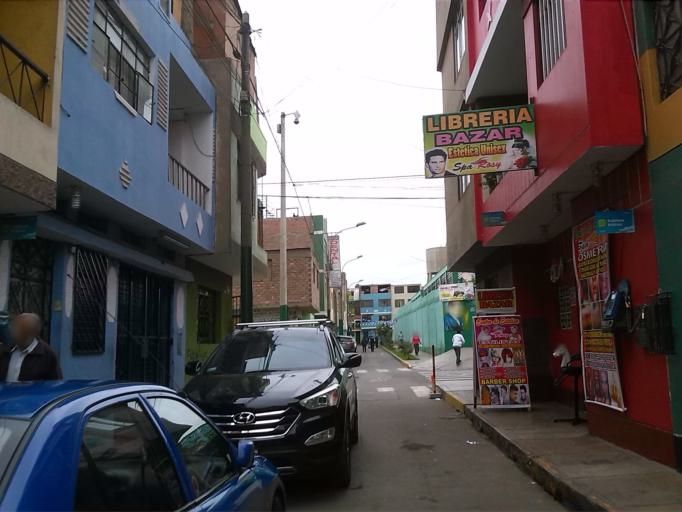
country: PE
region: Callao
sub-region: Callao
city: Callao
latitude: -12.0432
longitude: -77.0976
